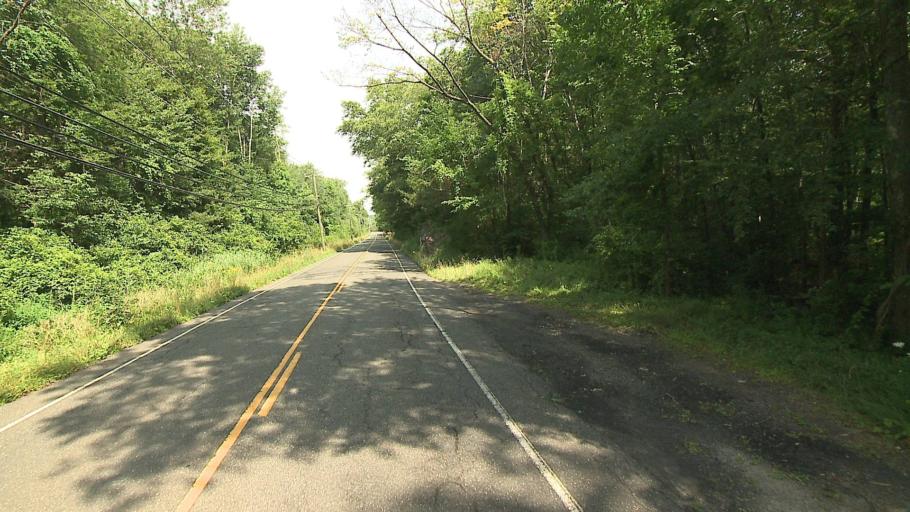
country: US
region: Connecticut
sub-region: Fairfield County
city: Sherman
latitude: 41.5681
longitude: -73.4969
